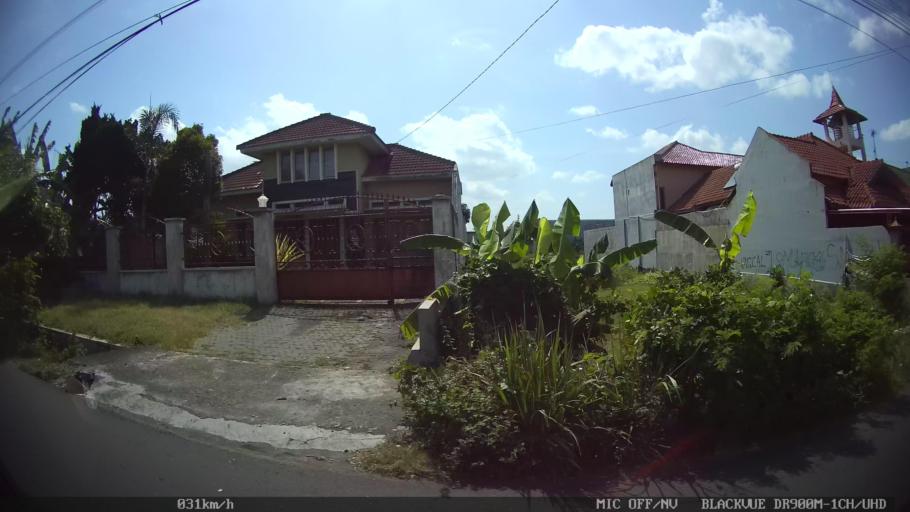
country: ID
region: Daerah Istimewa Yogyakarta
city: Yogyakarta
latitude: -7.8284
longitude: 110.3797
